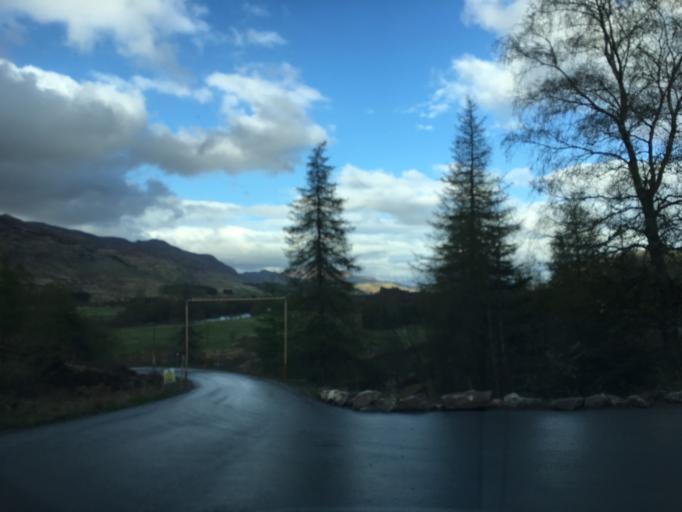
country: GB
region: Scotland
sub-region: Highland
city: Kingussie
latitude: 57.0100
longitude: -4.3340
